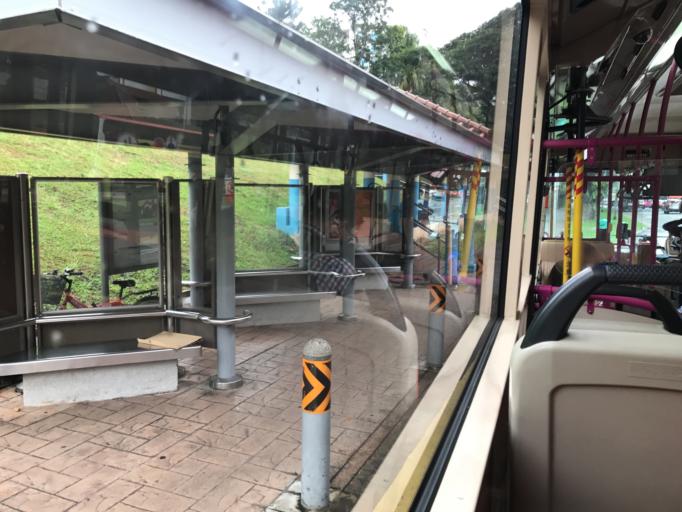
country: SG
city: Singapore
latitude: 1.3280
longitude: 103.9268
